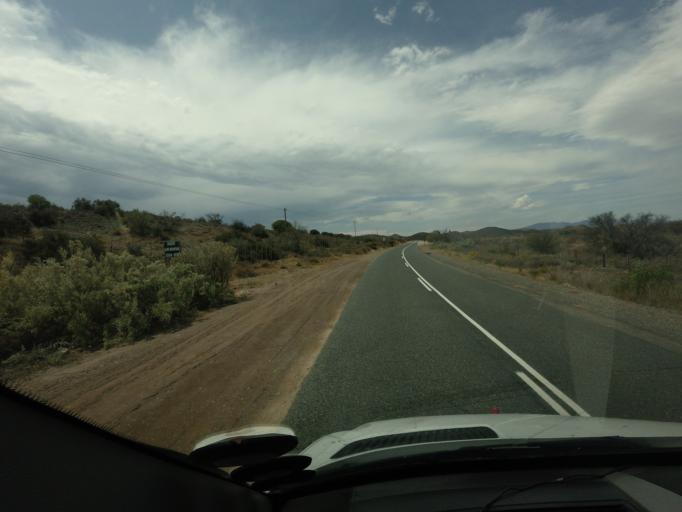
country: ZA
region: Western Cape
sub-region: Eden District Municipality
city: Ladismith
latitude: -33.6494
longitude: 21.0173
